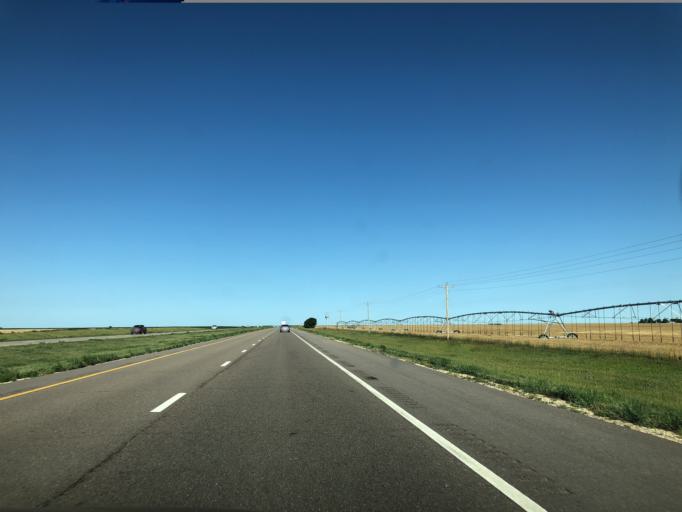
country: US
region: Kansas
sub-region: Sherman County
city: Goodland
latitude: 39.3301
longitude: -101.5635
